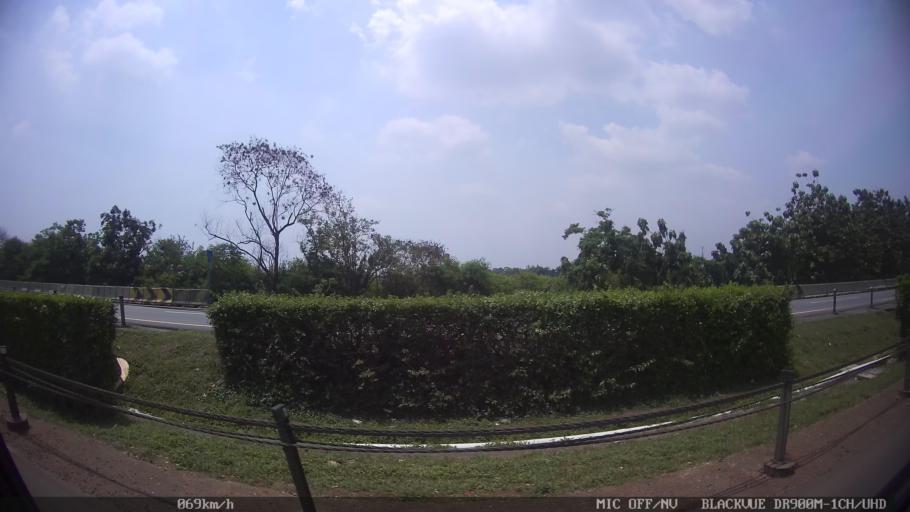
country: ID
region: West Java
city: Kresek
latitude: -6.1436
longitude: 106.2771
